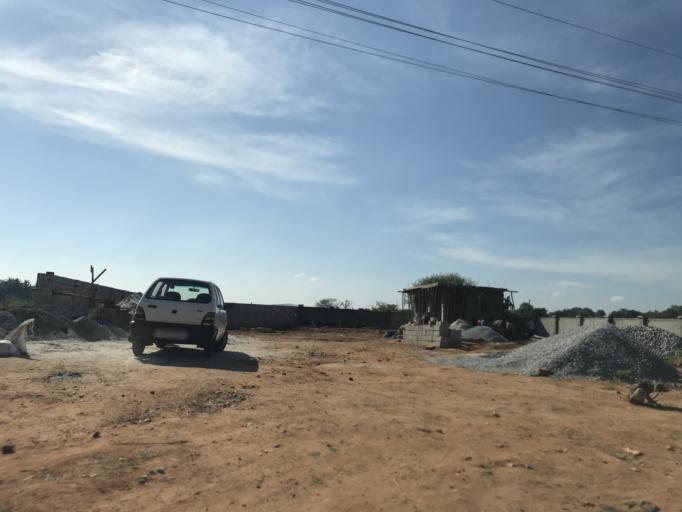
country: IN
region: Karnataka
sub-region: Mysore
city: Sargur
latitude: 12.1220
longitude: 76.4863
